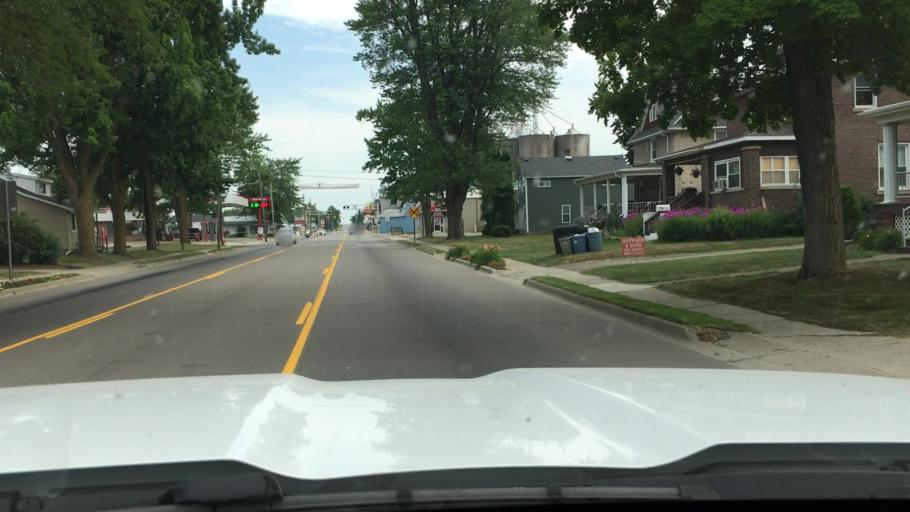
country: US
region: Michigan
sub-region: Sanilac County
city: Marlette
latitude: 43.3240
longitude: -83.0799
